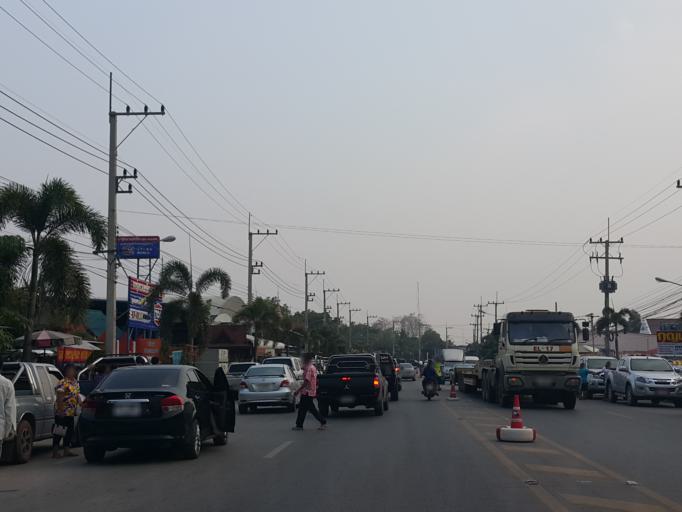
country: TH
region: Uthai Thani
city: Huai Khot
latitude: 15.1811
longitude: 99.6972
